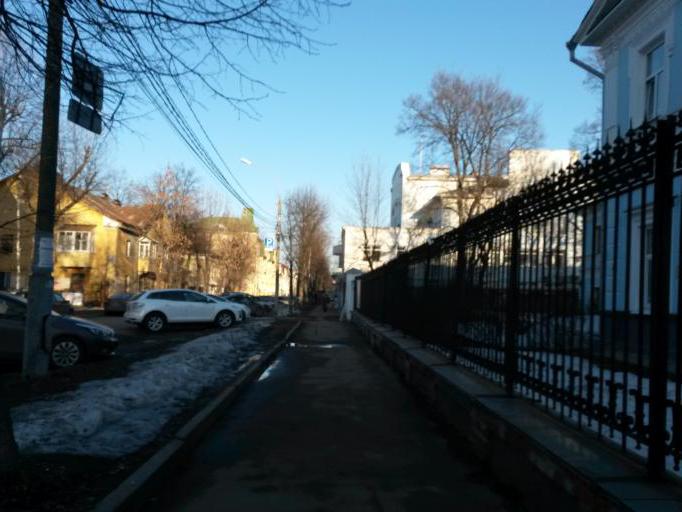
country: RU
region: Jaroslavl
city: Yaroslavl
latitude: 57.6324
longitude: 39.8734
